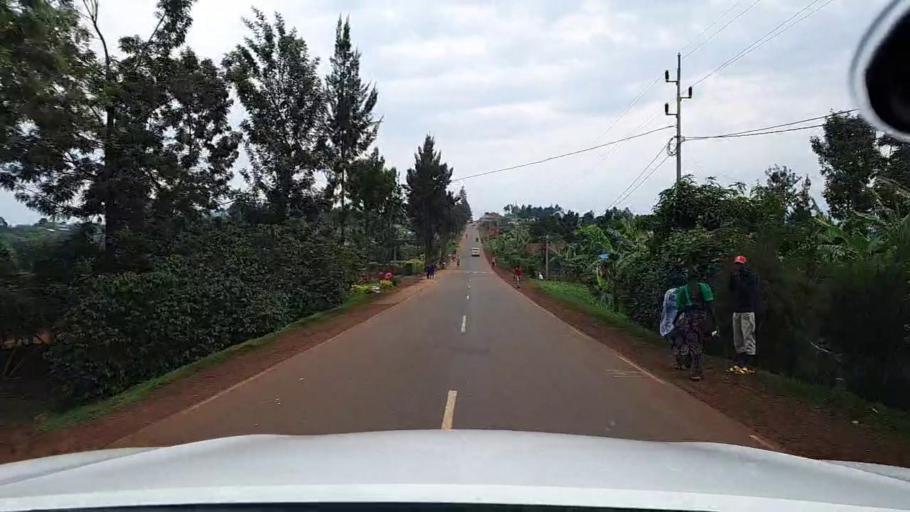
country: RW
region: Western Province
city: Cyangugu
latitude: -2.6316
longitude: 28.9518
